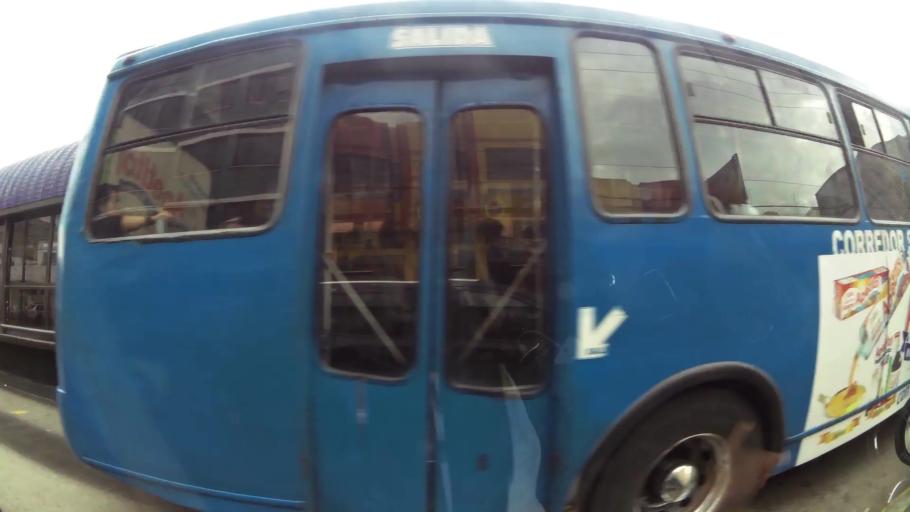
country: EC
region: Pichincha
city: Quito
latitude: -0.2614
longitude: -78.5473
